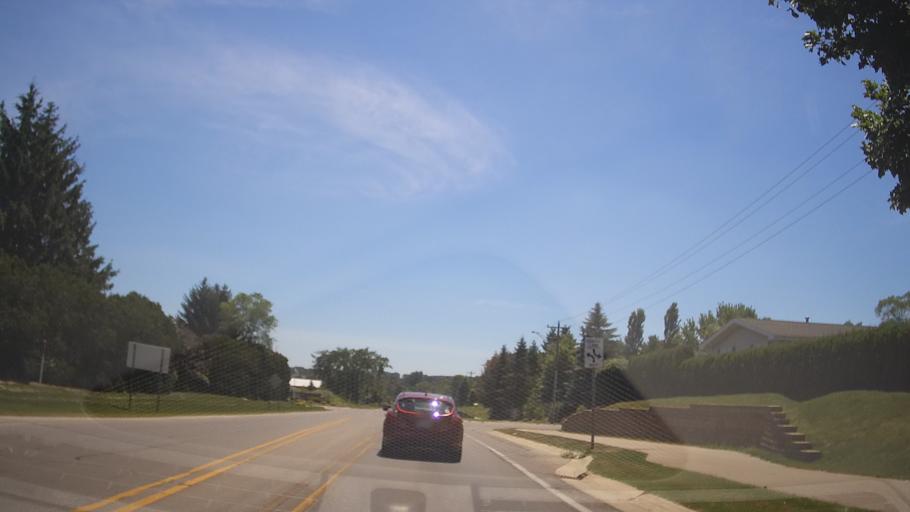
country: US
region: Michigan
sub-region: Grand Traverse County
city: Traverse City
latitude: 44.7412
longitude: -85.6558
